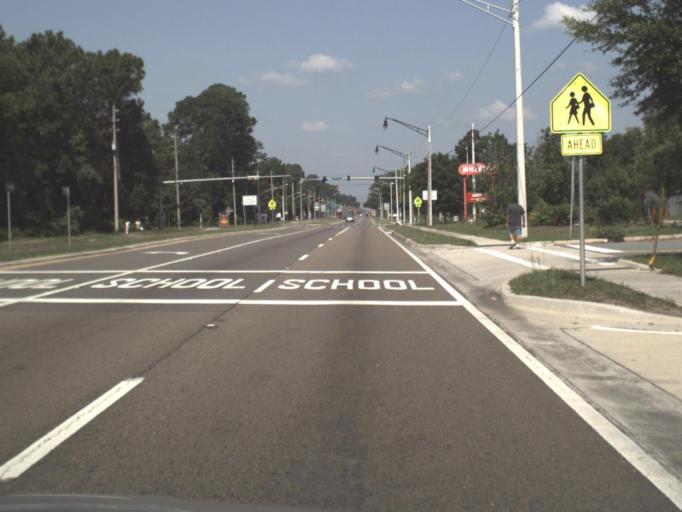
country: US
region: Florida
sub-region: Clay County
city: Bellair-Meadowbrook Terrace
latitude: 30.2477
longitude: -81.8221
